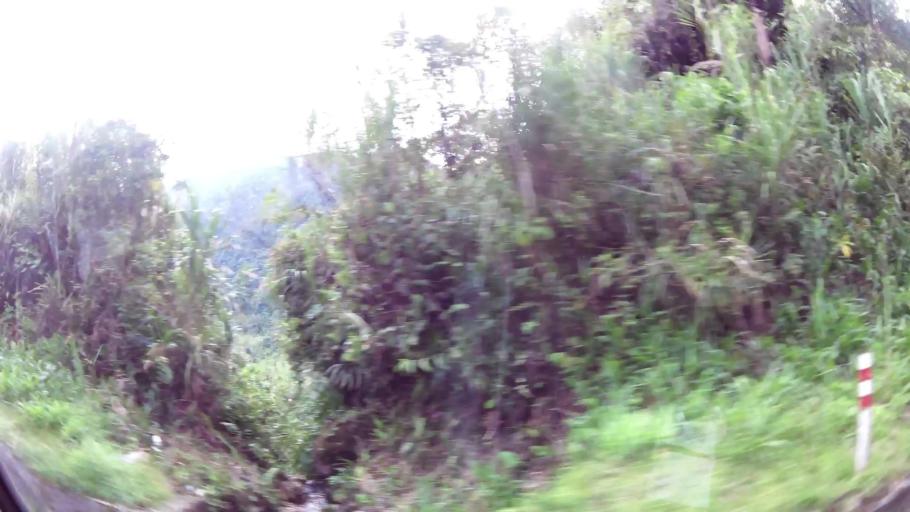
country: EC
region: Pastaza
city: Puyo
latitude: -1.4346
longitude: -78.1780
